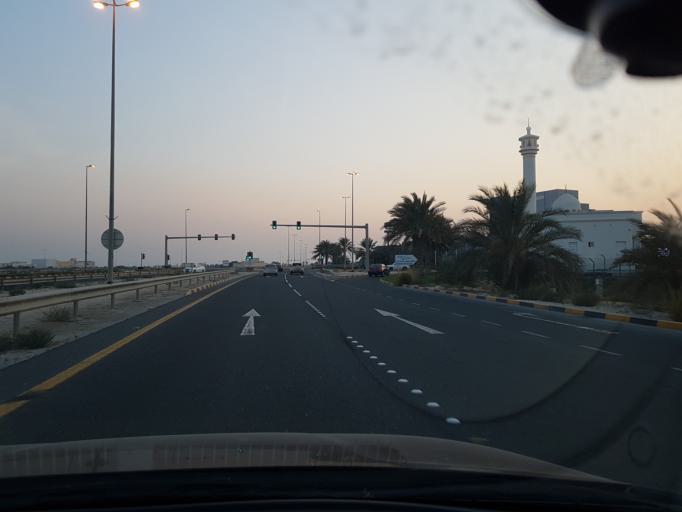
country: BH
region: Central Governorate
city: Dar Kulayb
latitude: 26.0282
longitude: 50.4972
